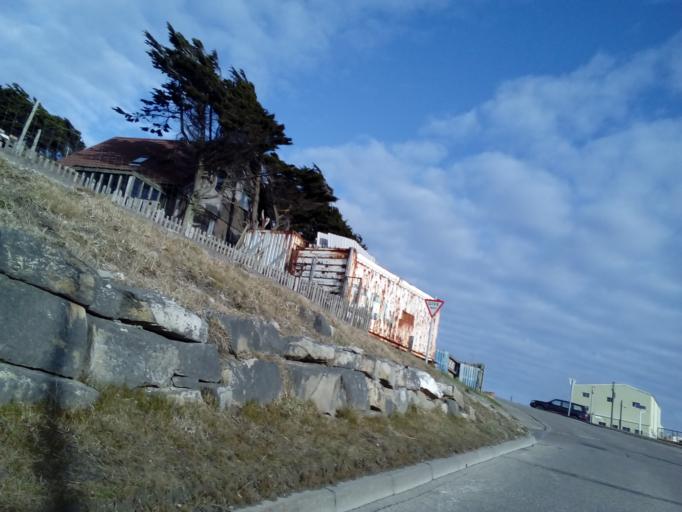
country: FK
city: Stanley
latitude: -51.6931
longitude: -57.8703
